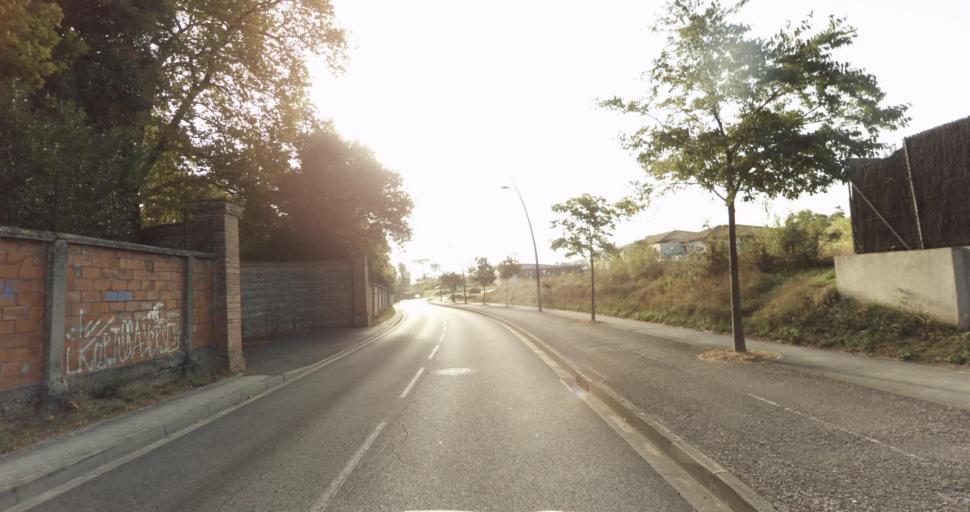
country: FR
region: Midi-Pyrenees
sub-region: Departement de la Haute-Garonne
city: Ramonville-Saint-Agne
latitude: 43.5375
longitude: 1.4672
